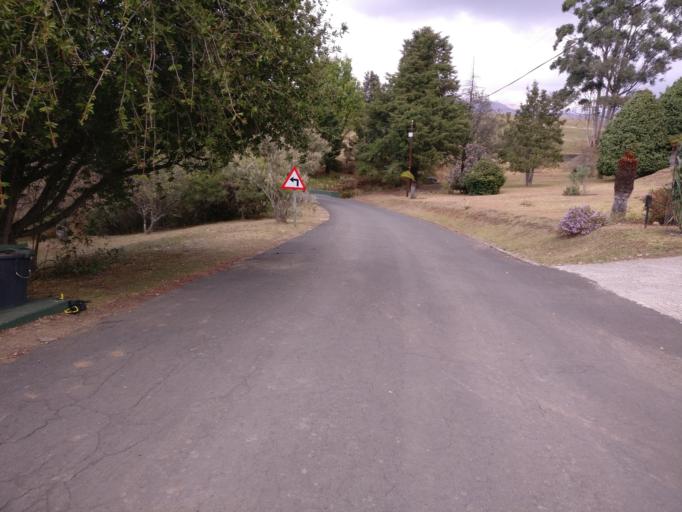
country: ZA
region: KwaZulu-Natal
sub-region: uThukela District Municipality
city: Bergville
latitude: -29.0132
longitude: 29.4157
